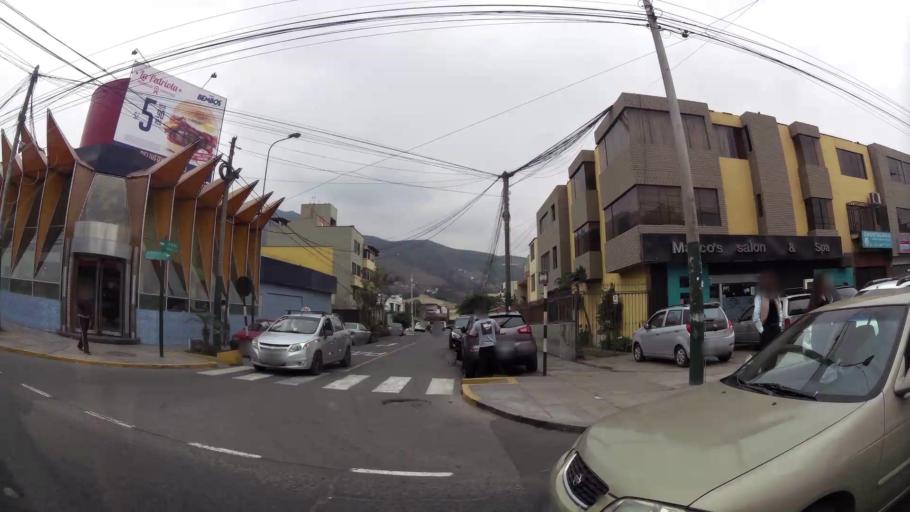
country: PE
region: Lima
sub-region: Lima
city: La Molina
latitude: -12.1090
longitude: -76.9706
